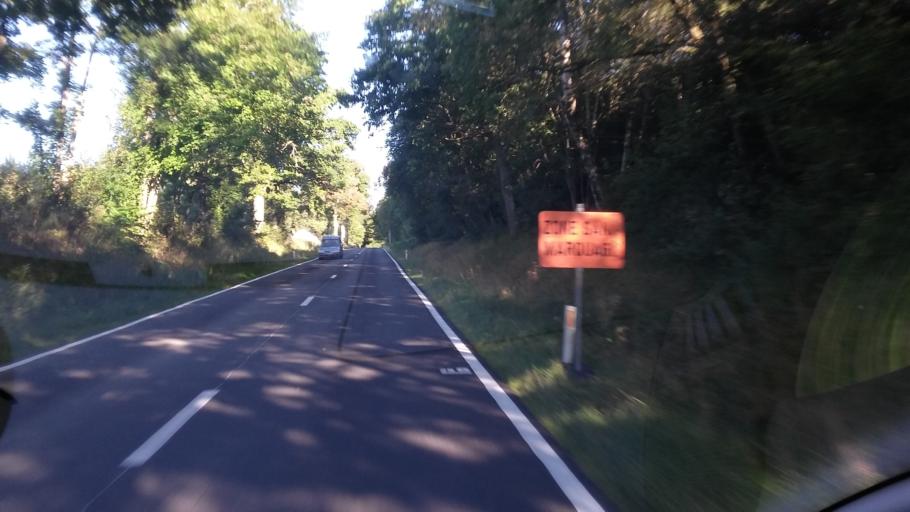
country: BE
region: Wallonia
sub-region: Province du Luxembourg
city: Leglise
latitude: 49.8129
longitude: 5.5044
